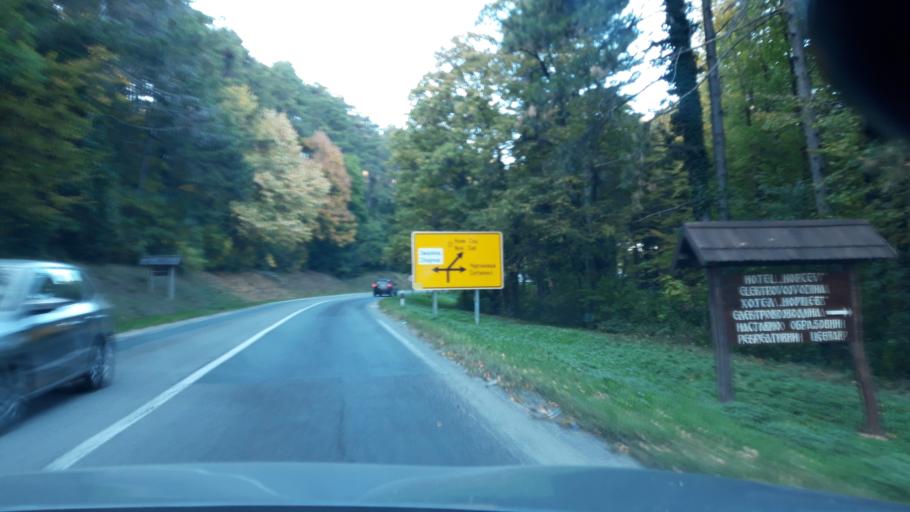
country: RS
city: Vrdnik
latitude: 45.1480
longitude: 19.8294
